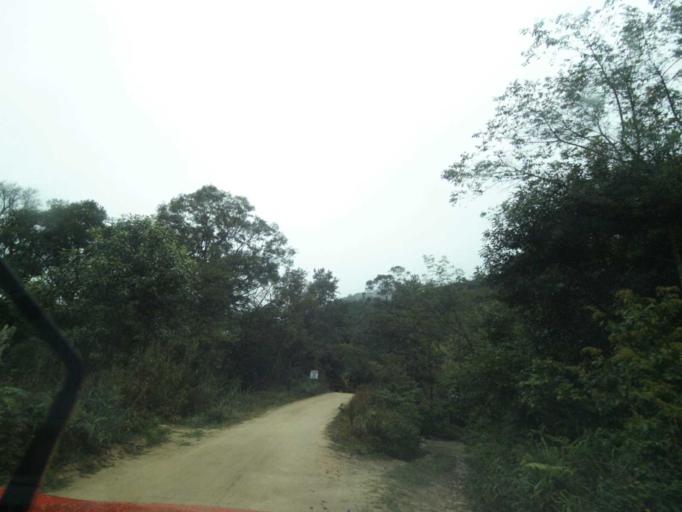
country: BR
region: Santa Catarina
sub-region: Anitapolis
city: Anitapolis
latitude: -27.9202
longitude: -49.1923
